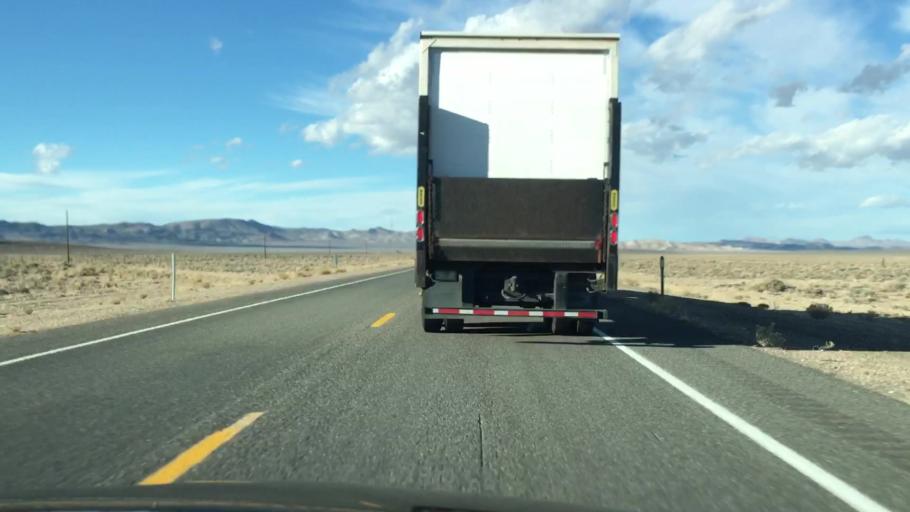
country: US
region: Nevada
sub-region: Esmeralda County
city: Goldfield
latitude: 37.4376
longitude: -117.1633
